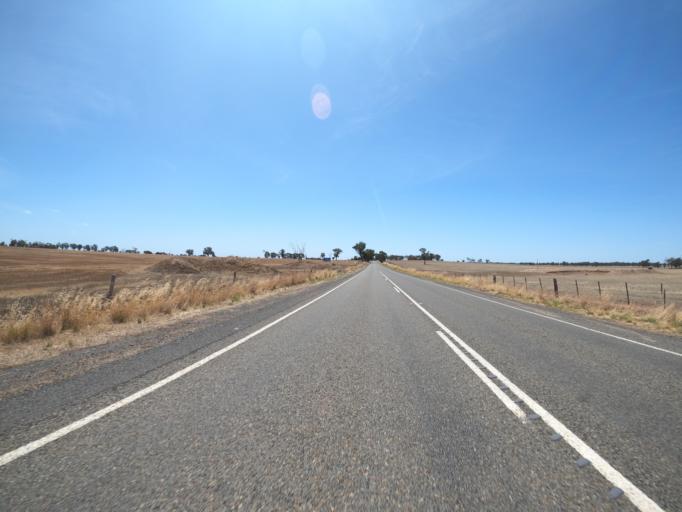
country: AU
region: Victoria
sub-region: Moira
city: Yarrawonga
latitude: -36.0955
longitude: 145.9955
